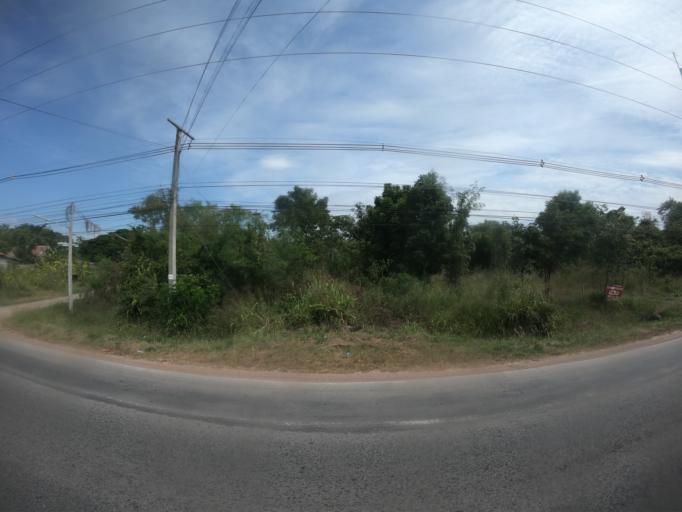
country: TH
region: Maha Sarakham
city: Chiang Yuen
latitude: 16.4274
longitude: 103.0652
